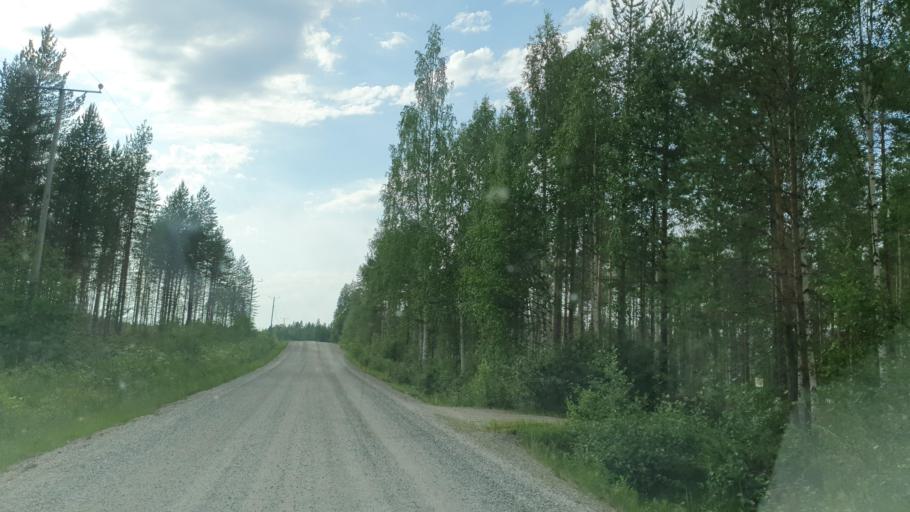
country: FI
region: Kainuu
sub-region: Kehys-Kainuu
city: Kuhmo
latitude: 64.0885
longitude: 29.6610
